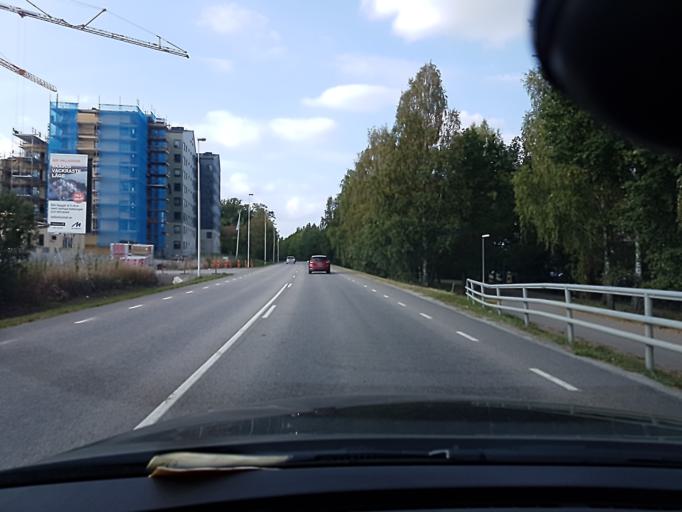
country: SE
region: Kronoberg
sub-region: Vaxjo Kommun
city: Vaexjoe
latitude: 56.8610
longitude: 14.8092
